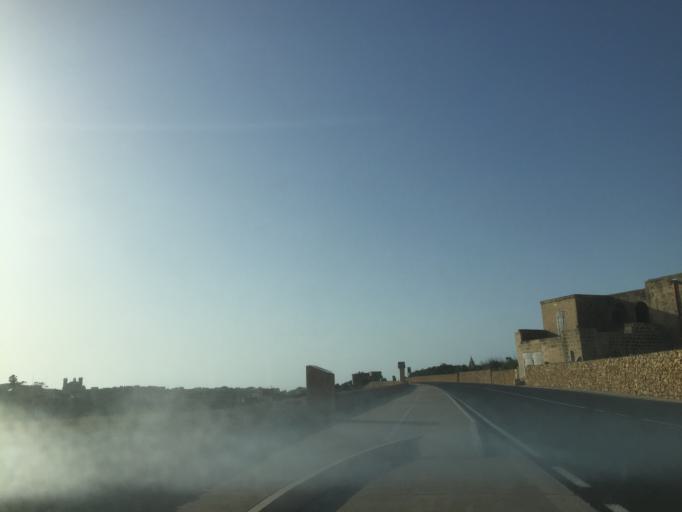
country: MT
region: L-Gharb
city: Gharb
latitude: 36.0555
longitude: 14.2176
